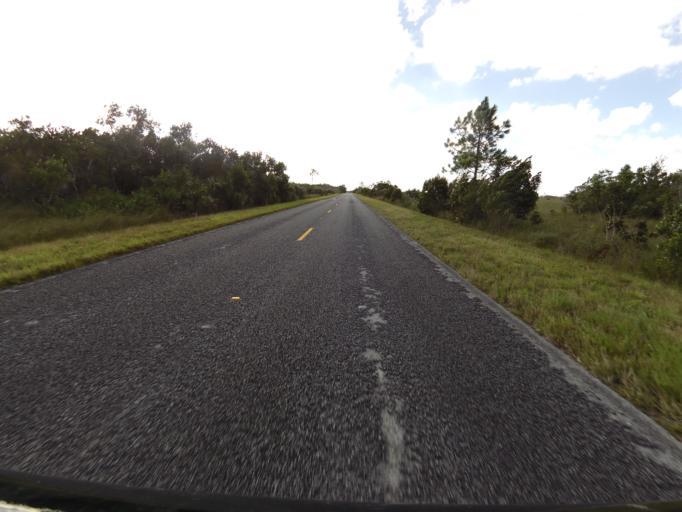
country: US
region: Florida
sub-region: Miami-Dade County
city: Florida City
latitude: 25.3965
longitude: -80.7968
